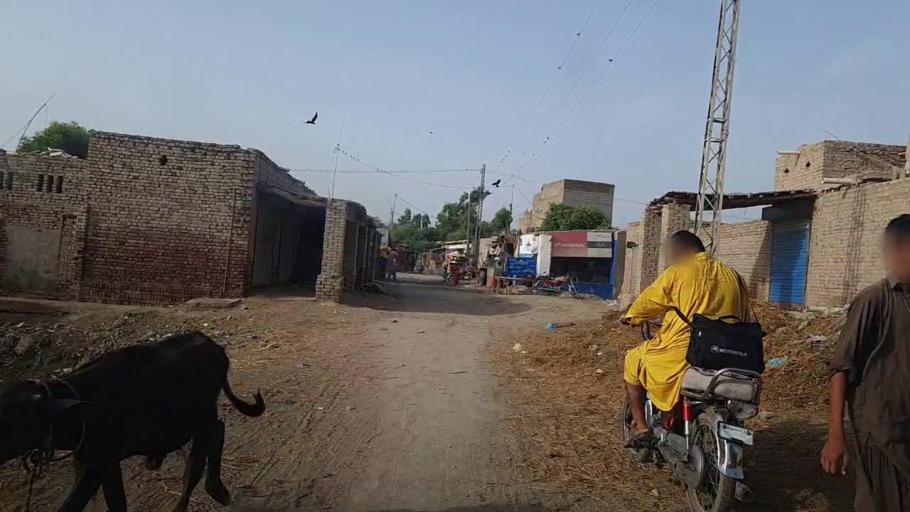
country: PK
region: Sindh
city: Khairpur Nathan Shah
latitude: 27.1142
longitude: 67.7885
